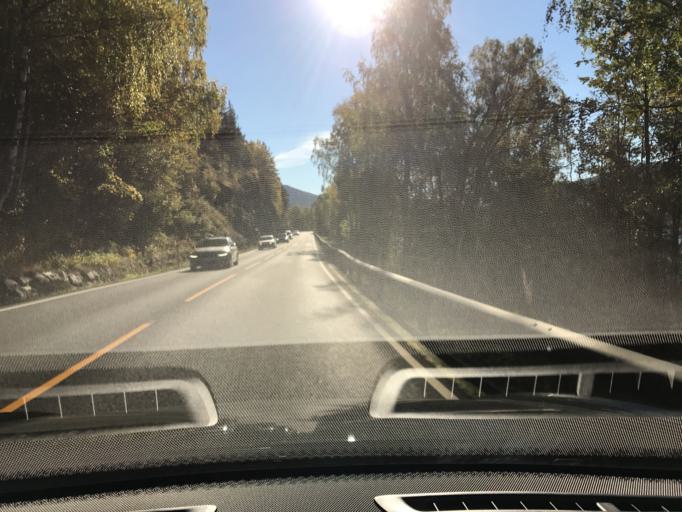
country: NO
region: Buskerud
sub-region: Krodsherad
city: Noresund
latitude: 60.3043
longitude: 9.6784
